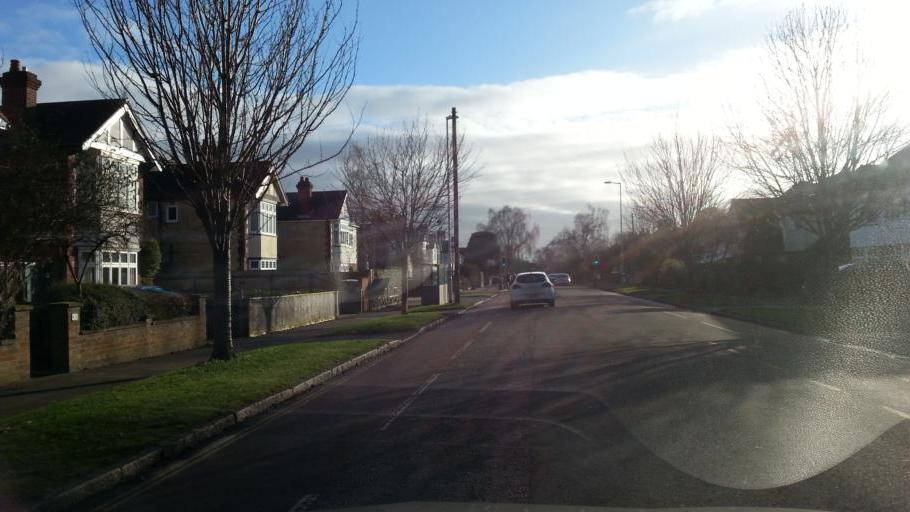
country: GB
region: England
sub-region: Cambridgeshire
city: Cambridge
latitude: 52.2194
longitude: 0.1218
